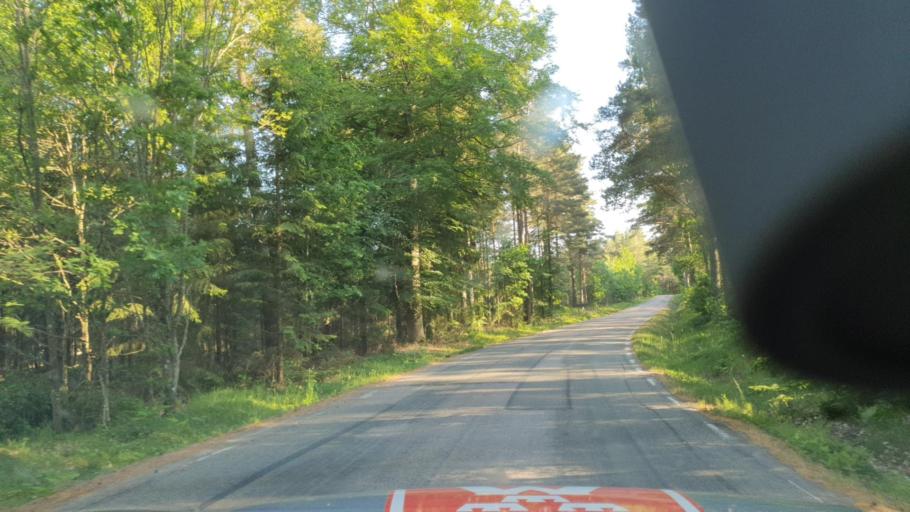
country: SE
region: Kalmar
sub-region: Torsas Kommun
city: Torsas
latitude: 56.4944
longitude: 16.1032
